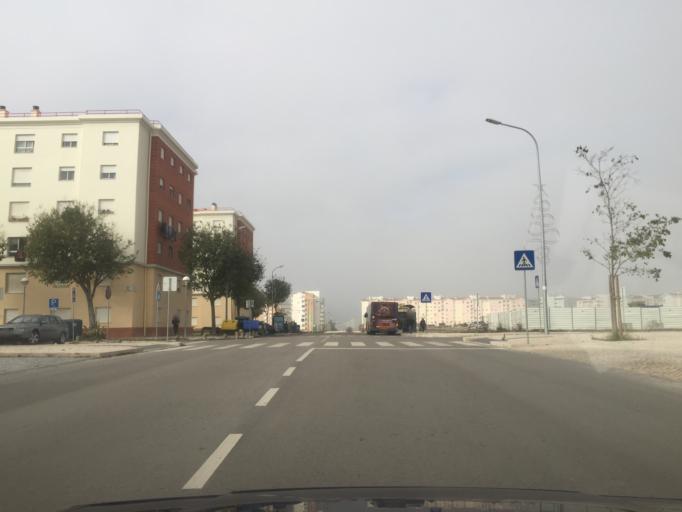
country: PT
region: Lisbon
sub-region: Odivelas
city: Olival do Basto
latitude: 38.7790
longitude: -9.1435
